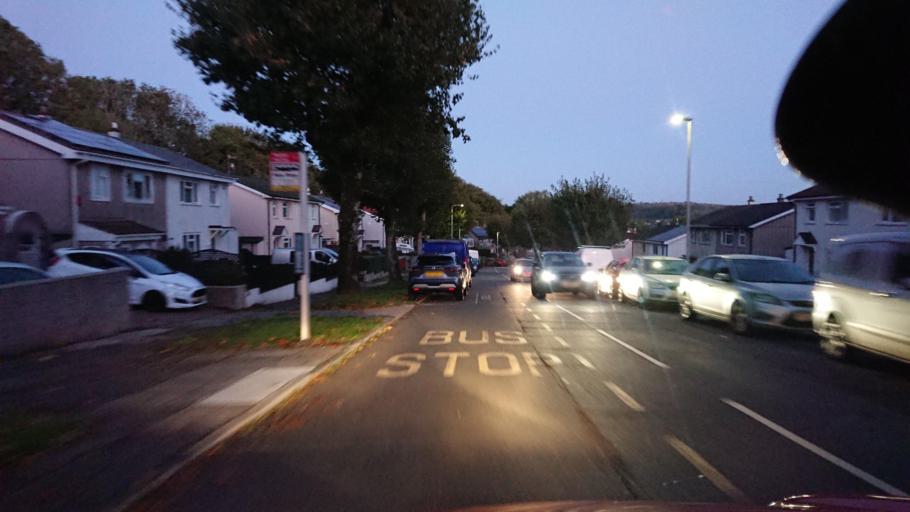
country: GB
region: England
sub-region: Plymouth
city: Plymstock
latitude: 50.3902
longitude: -4.0975
